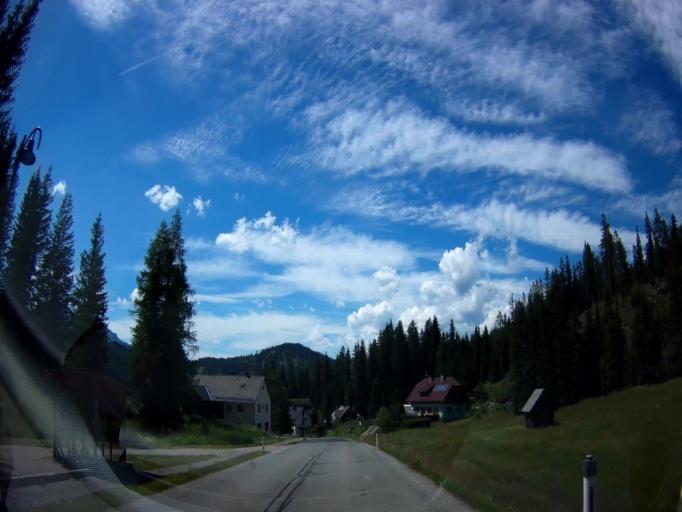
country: AT
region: Carinthia
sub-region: Politischer Bezirk Sankt Veit an der Glan
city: Glodnitz
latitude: 46.9415
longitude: 14.0359
